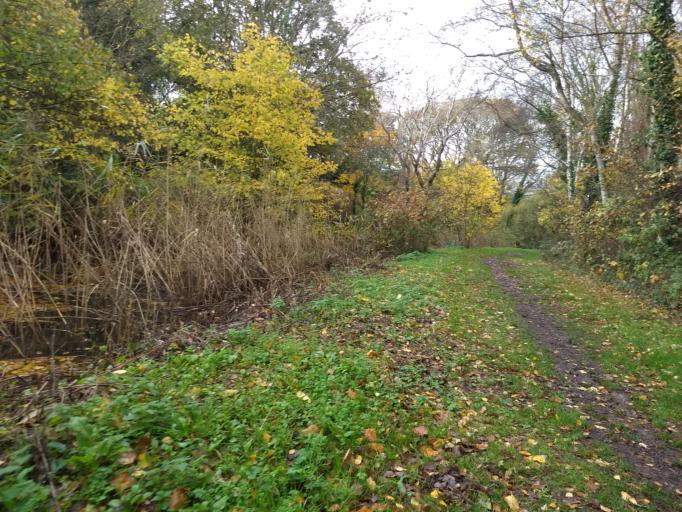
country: GB
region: England
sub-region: Isle of Wight
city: Freshwater
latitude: 50.6765
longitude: -1.5130
